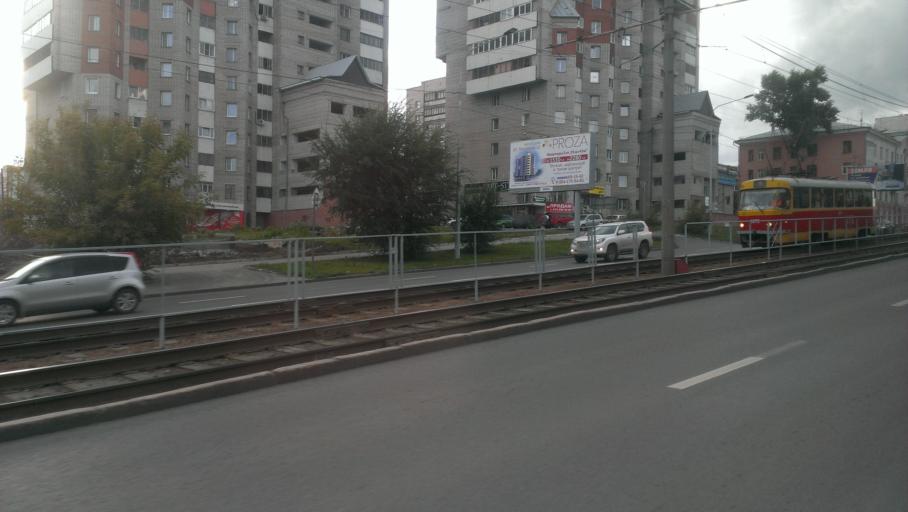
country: RU
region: Altai Krai
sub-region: Gorod Barnaulskiy
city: Barnaul
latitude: 53.3412
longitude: 83.7707
